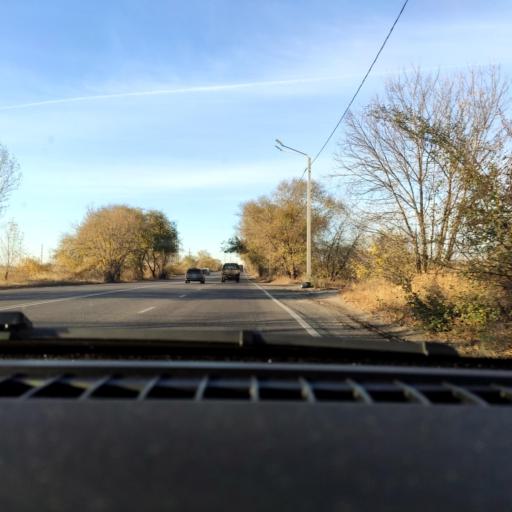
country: RU
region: Voronezj
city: Maslovka
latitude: 51.6260
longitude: 39.2829
